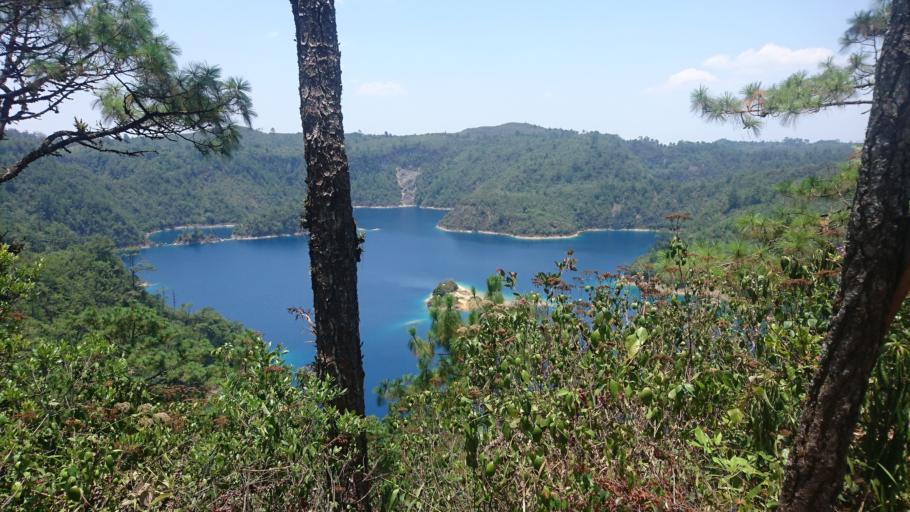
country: GT
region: Huehuetenango
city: Union
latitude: 16.1033
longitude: -91.6723
